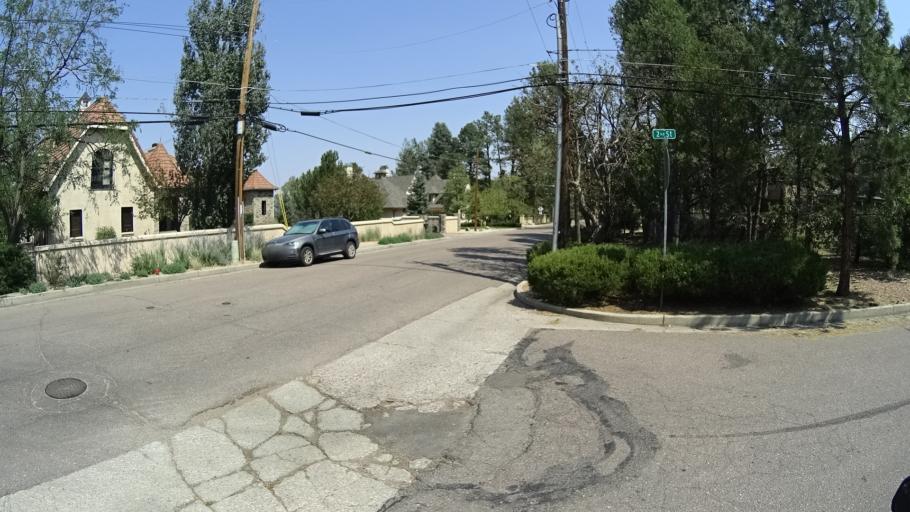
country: US
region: Colorado
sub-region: El Paso County
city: Colorado Springs
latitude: 38.7963
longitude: -104.8470
